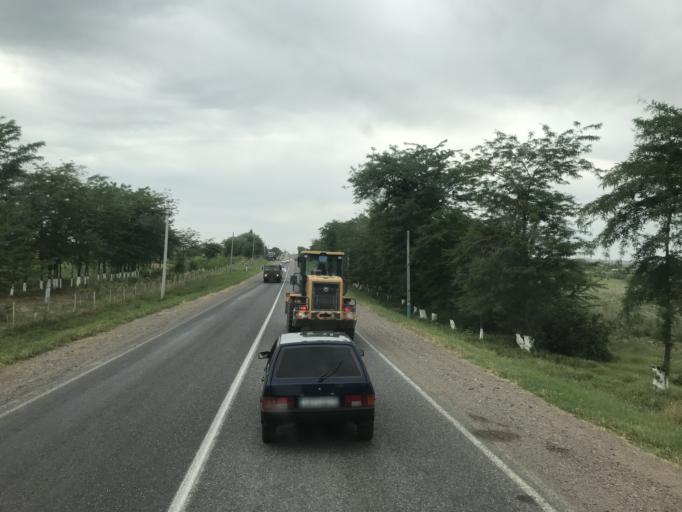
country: UZ
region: Toshkent
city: Salor
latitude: 41.4953
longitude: 69.3317
